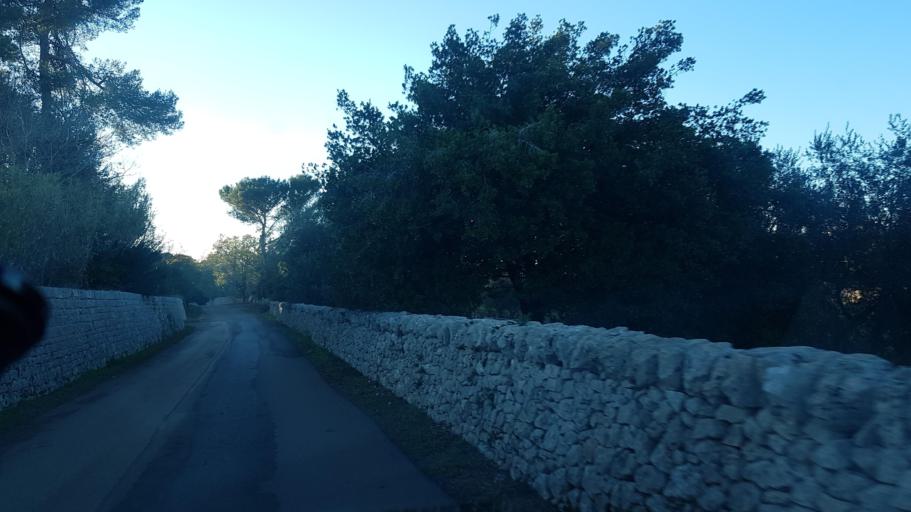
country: IT
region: Apulia
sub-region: Provincia di Brindisi
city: Ostuni
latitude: 40.7031
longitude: 17.5397
